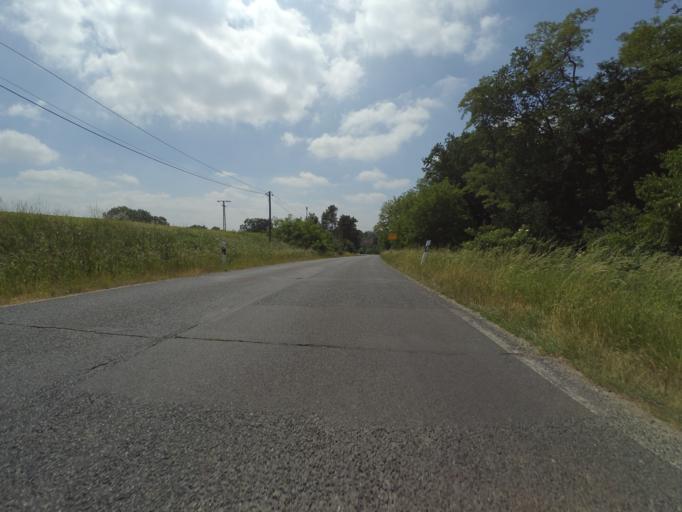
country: DE
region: Mecklenburg-Vorpommern
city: Plau am See
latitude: 53.4122
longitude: 12.3245
